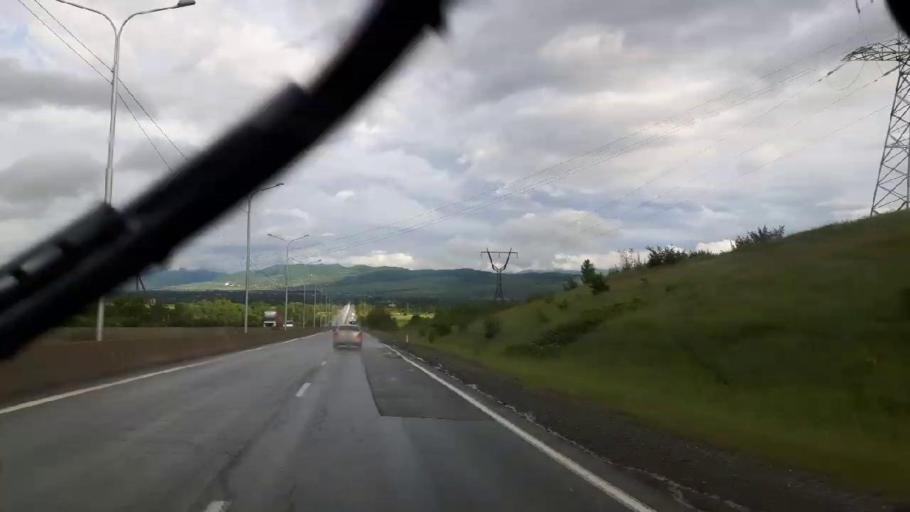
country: GE
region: Shida Kartli
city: Kaspi
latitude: 41.9279
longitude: 44.5322
